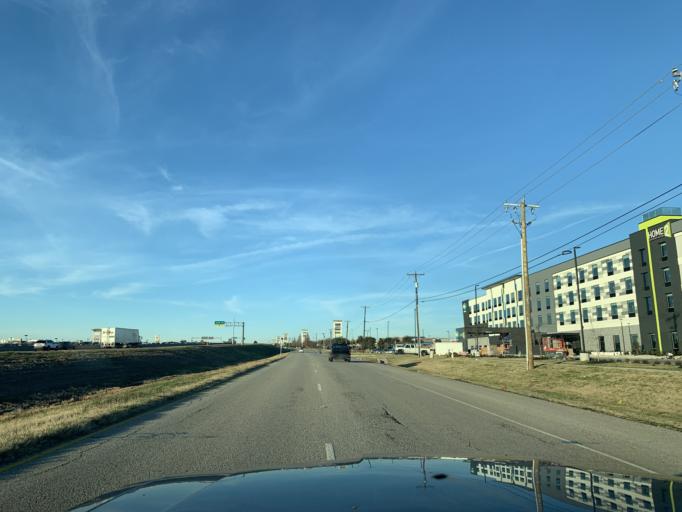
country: US
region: Texas
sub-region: Tarrant County
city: Euless
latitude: 32.8737
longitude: -97.0991
